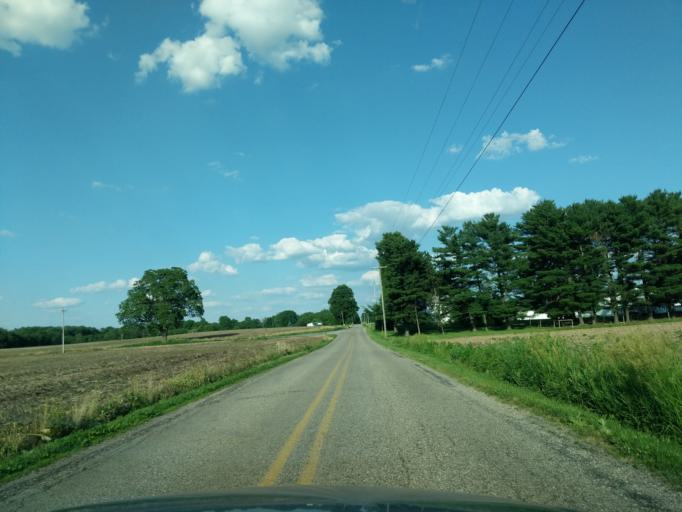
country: US
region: Indiana
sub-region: Kosciusko County
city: North Webster
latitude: 41.3025
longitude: -85.5841
